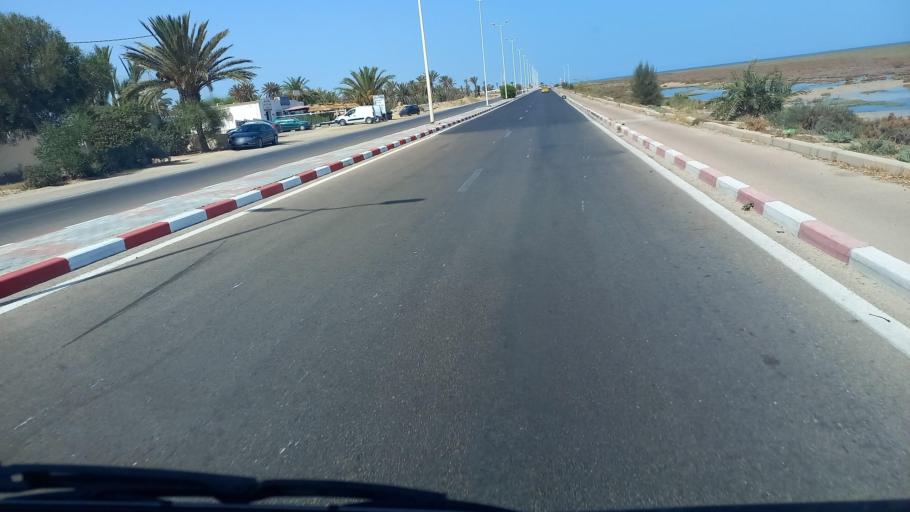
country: TN
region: Madanin
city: Houmt Souk
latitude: 33.8725
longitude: 10.9333
